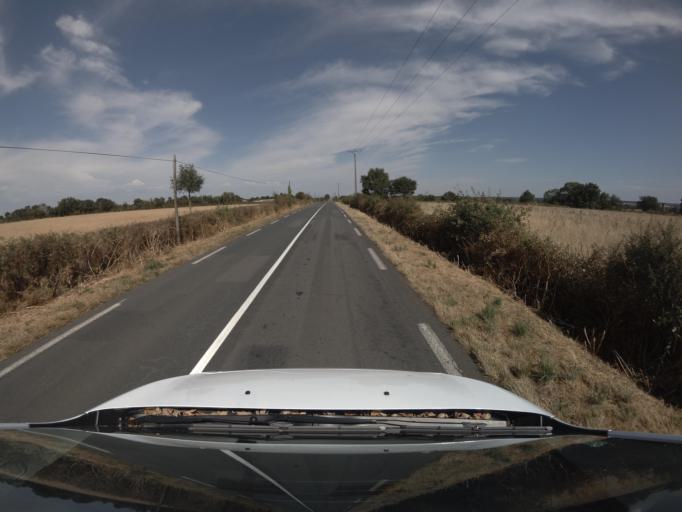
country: FR
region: Poitou-Charentes
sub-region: Departement des Deux-Sevres
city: Nueil-les-Aubiers
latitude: 46.9776
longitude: -0.5283
